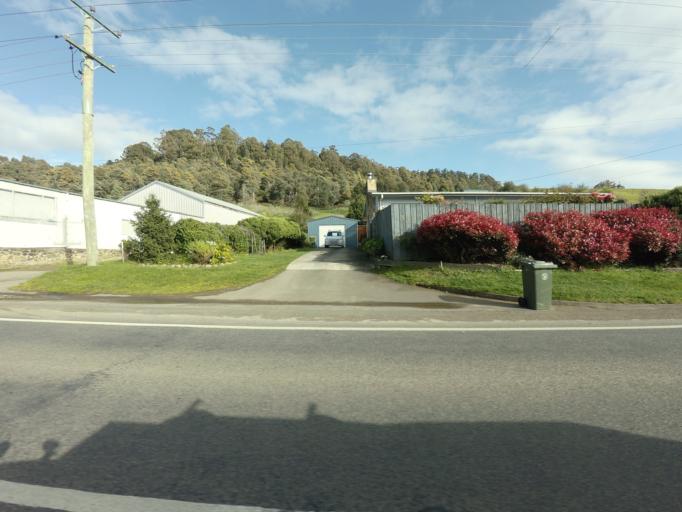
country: AU
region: Tasmania
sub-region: Huon Valley
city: Franklin
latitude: -43.0970
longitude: 147.0062
